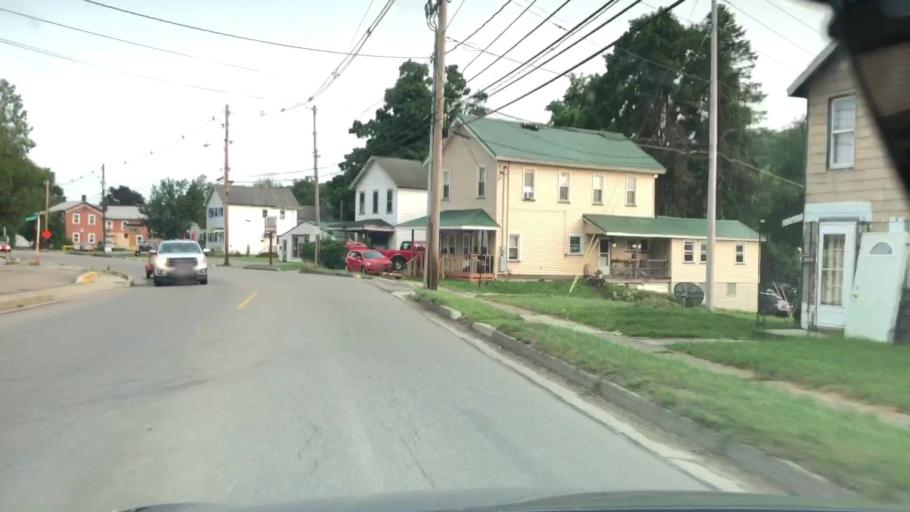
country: US
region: Pennsylvania
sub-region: Crawford County
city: Titusville
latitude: 41.6295
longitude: -79.6852
